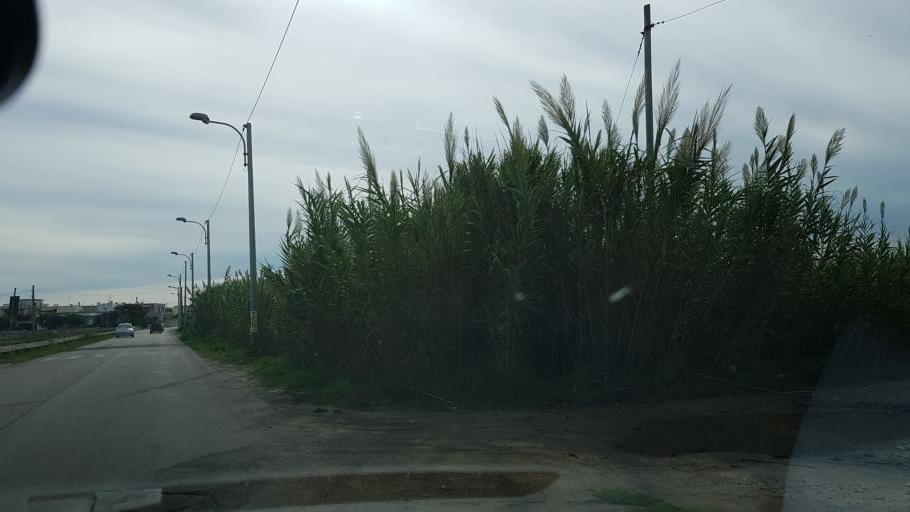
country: IT
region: Apulia
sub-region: Provincia di Lecce
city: Borgagne
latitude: 40.2942
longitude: 18.4189
